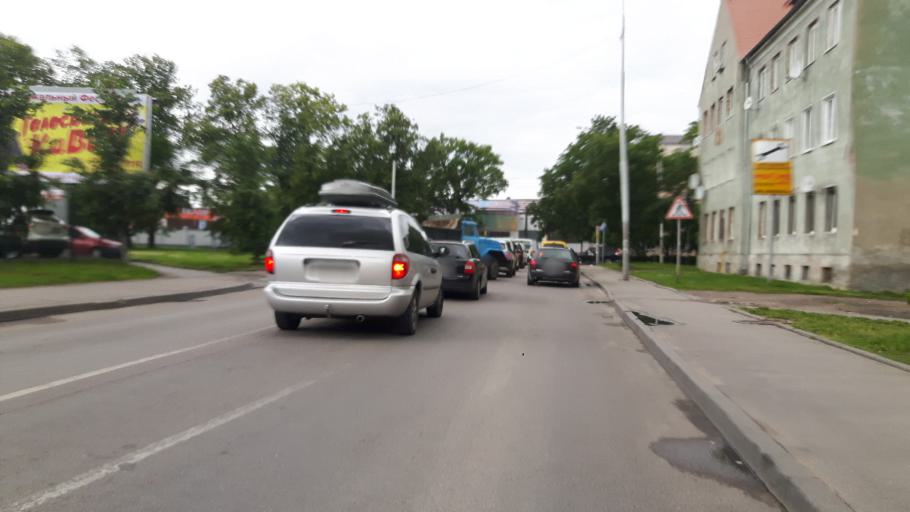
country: RU
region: Kaliningrad
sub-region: Gorod Kaliningrad
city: Kaliningrad
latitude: 54.7352
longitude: 20.4986
